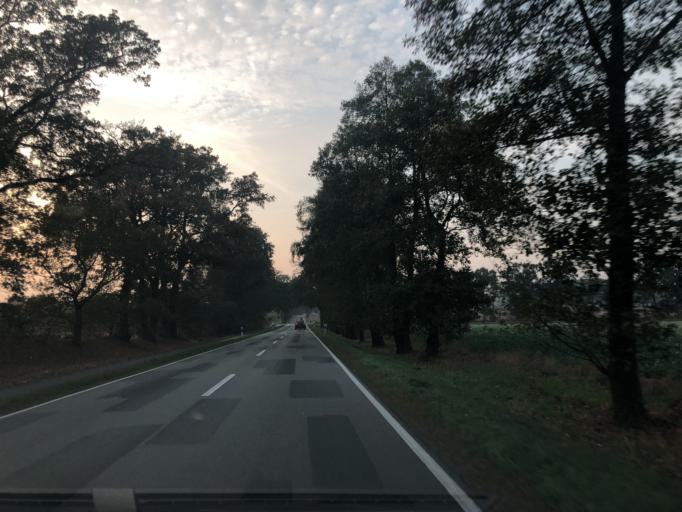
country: DE
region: Lower Saxony
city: Bosel
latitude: 53.0017
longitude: 7.9858
